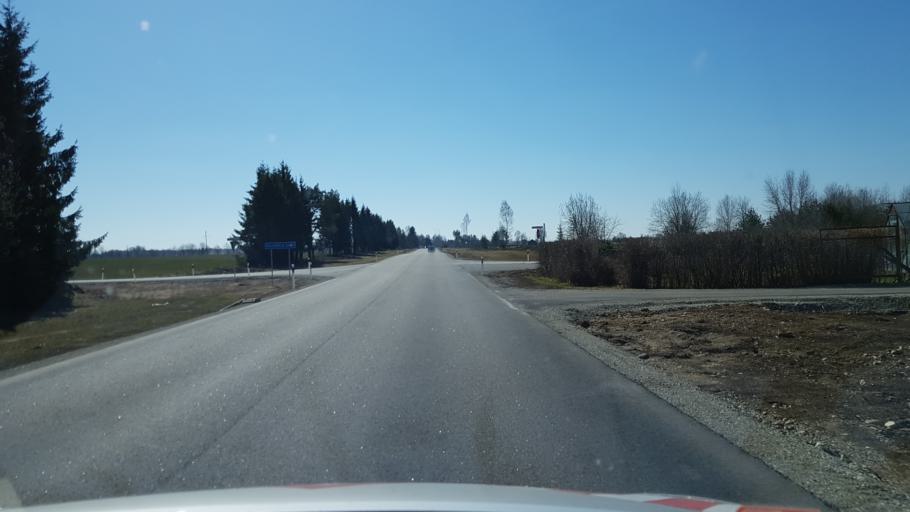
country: EE
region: Laeaene-Virumaa
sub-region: Vinni vald
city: Vinni
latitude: 59.1155
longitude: 26.6172
